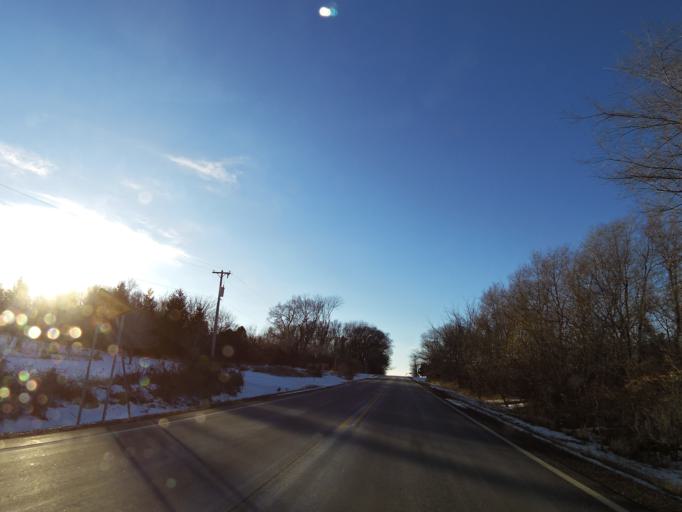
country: US
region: Minnesota
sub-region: Dakota County
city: Hastings
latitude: 44.7901
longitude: -92.8450
